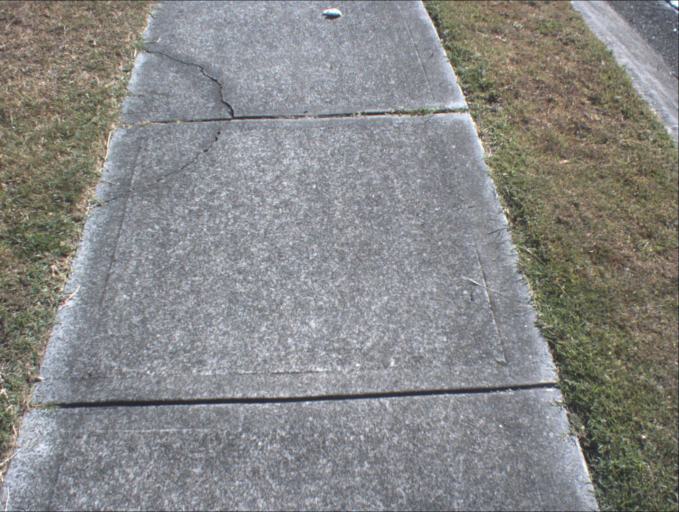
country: AU
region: Queensland
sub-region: Logan
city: Windaroo
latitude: -27.7202
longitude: 153.1825
